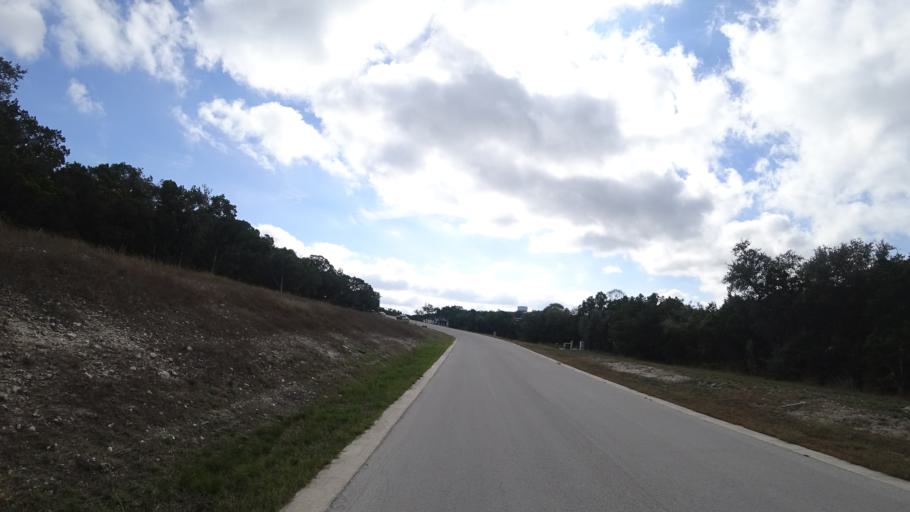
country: US
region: Texas
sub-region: Travis County
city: Bee Cave
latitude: 30.2544
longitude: -97.9280
